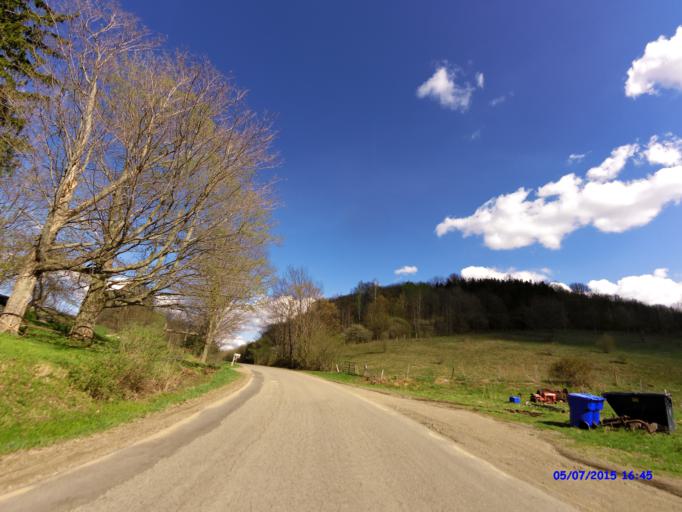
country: US
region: New York
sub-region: Cattaraugus County
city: Little Valley
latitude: 42.2847
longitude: -78.7152
